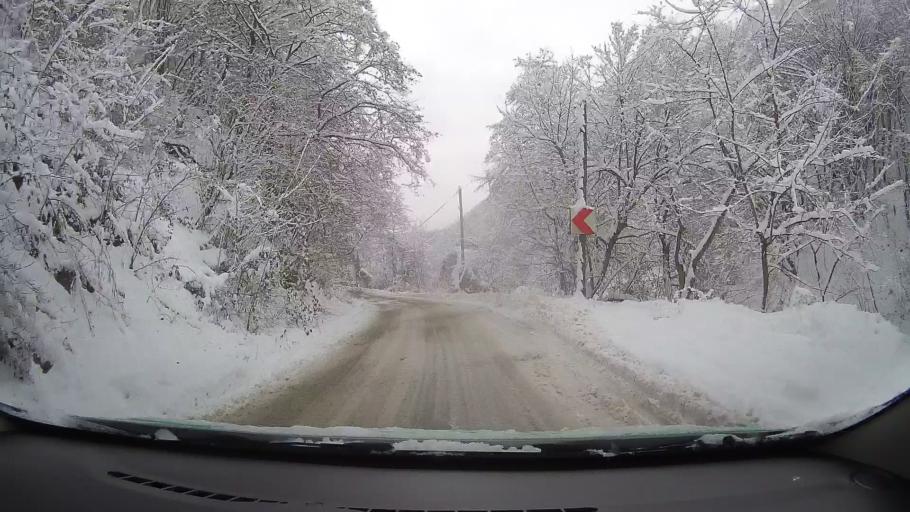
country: RO
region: Alba
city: Pianu de Sus
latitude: 45.8694
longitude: 23.4953
